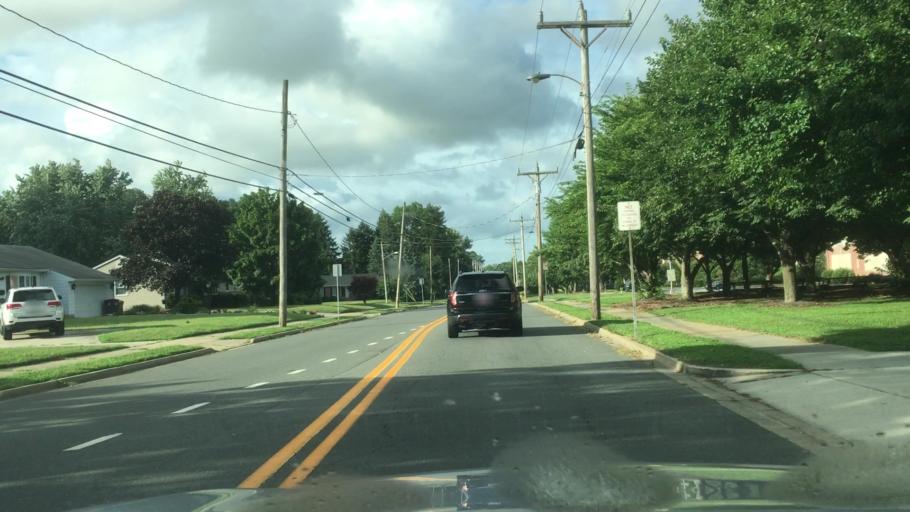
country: US
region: Delaware
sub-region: Sussex County
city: Milford
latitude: 38.9042
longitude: -75.4377
